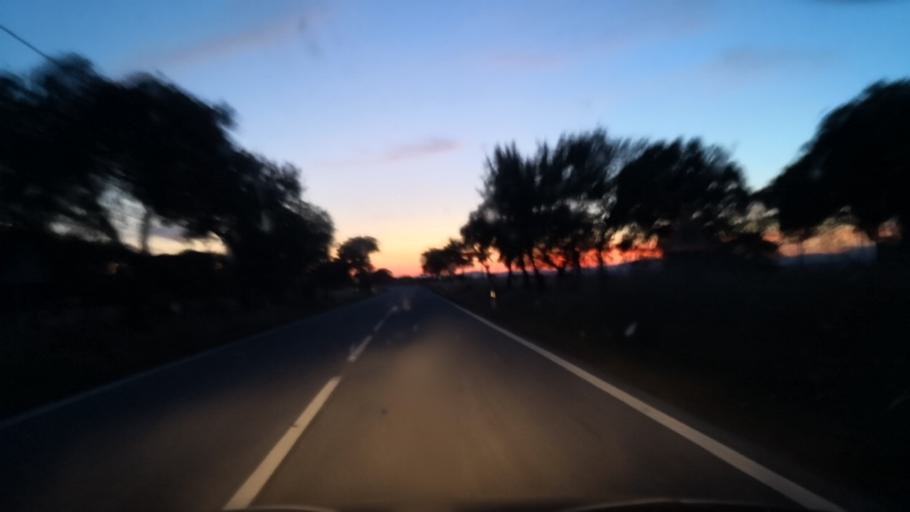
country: ES
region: Extremadura
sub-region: Provincia de Caceres
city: Piedras Albas
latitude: 39.8537
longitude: -7.0522
